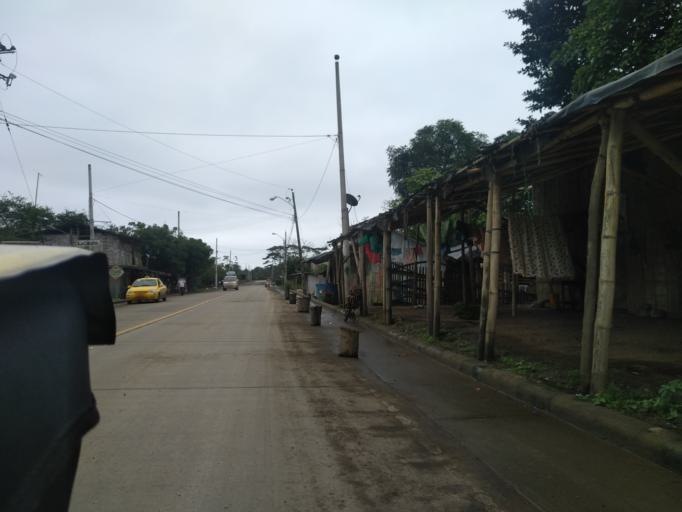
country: EC
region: Manabi
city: Jipijapa
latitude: -1.6717
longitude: -80.8085
